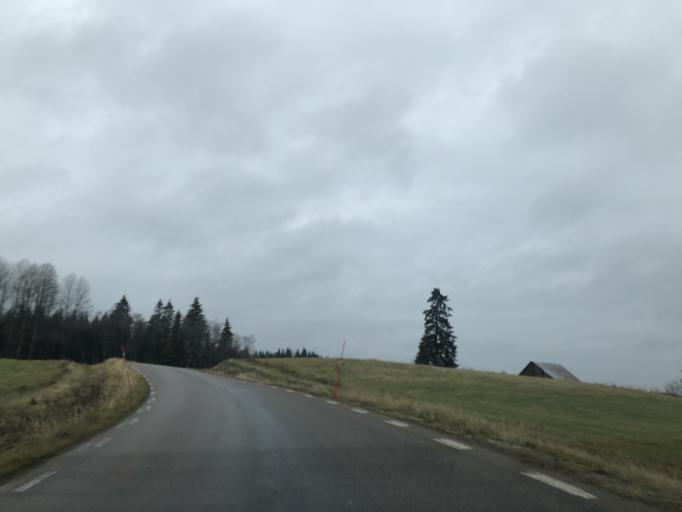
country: SE
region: Vaestra Goetaland
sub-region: Ulricehamns Kommun
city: Ulricehamn
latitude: 57.8893
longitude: 13.5115
